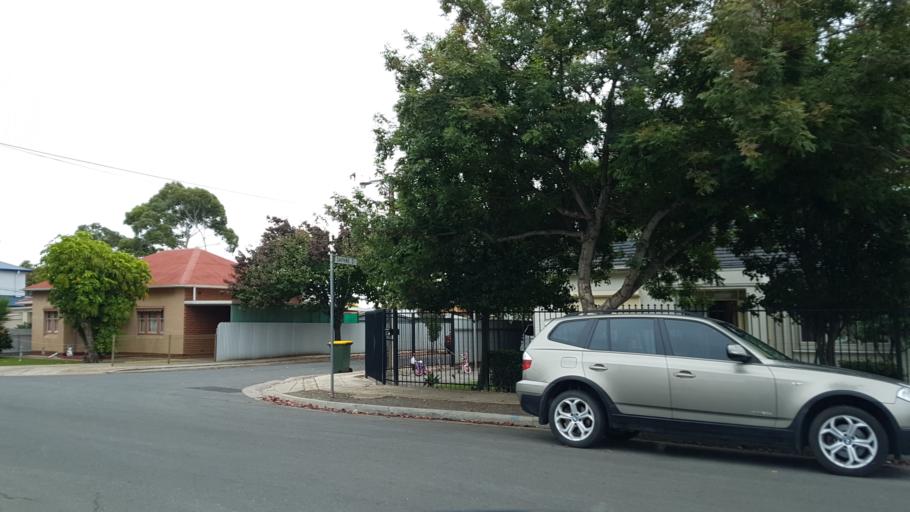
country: AU
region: South Australia
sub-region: Unley
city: Forestville
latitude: -34.9522
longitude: 138.5681
